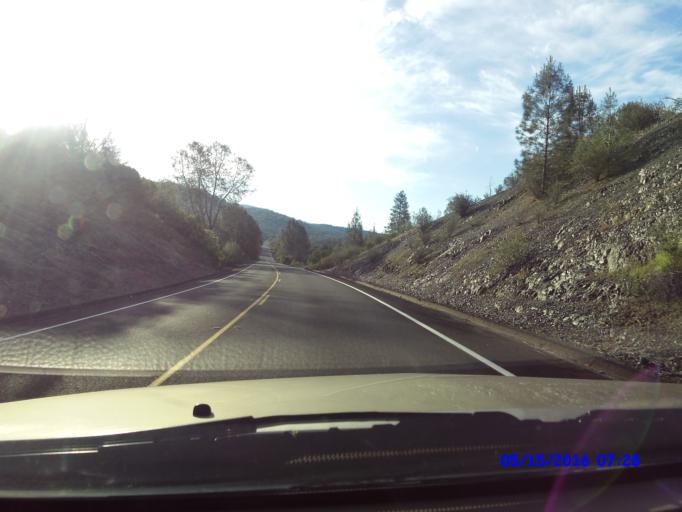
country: US
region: California
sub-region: Tuolumne County
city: Tuolumne City
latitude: 37.7356
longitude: -120.2287
